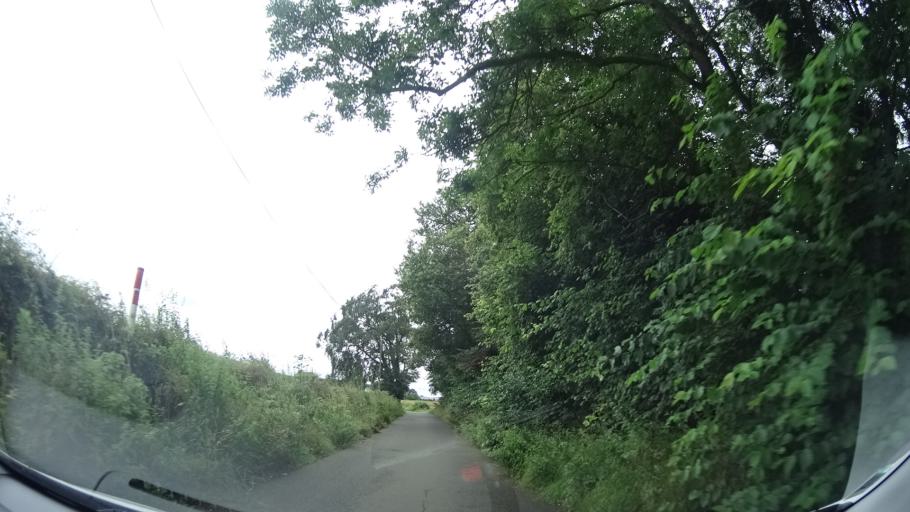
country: GB
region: Scotland
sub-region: West Lothian
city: Kirknewton
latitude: 55.9166
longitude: -3.4310
